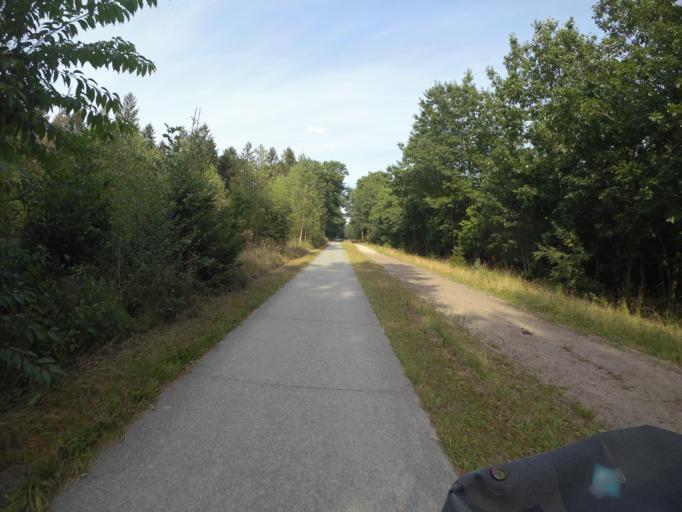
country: NL
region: Drenthe
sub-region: Gemeente Westerveld
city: Dwingeloo
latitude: 52.8964
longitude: 6.3612
